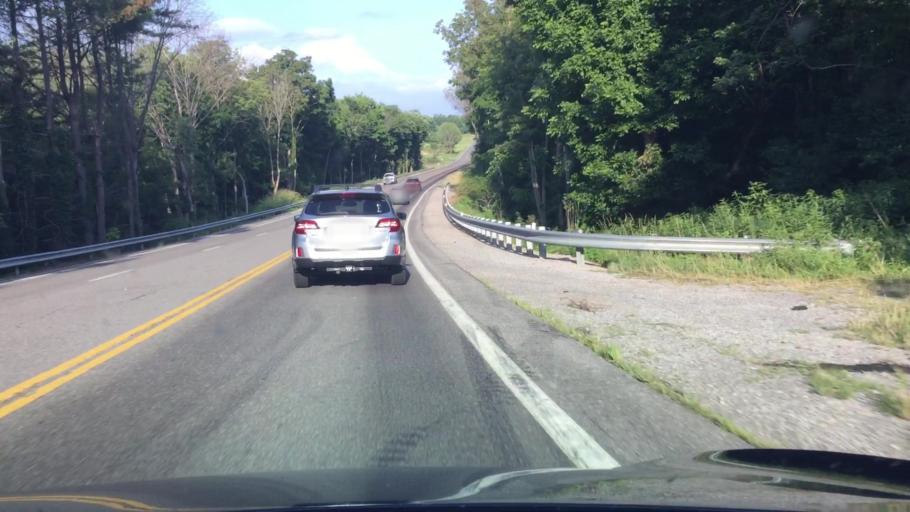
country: US
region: Virginia
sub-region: Montgomery County
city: Christiansburg
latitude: 37.1326
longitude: -80.4595
